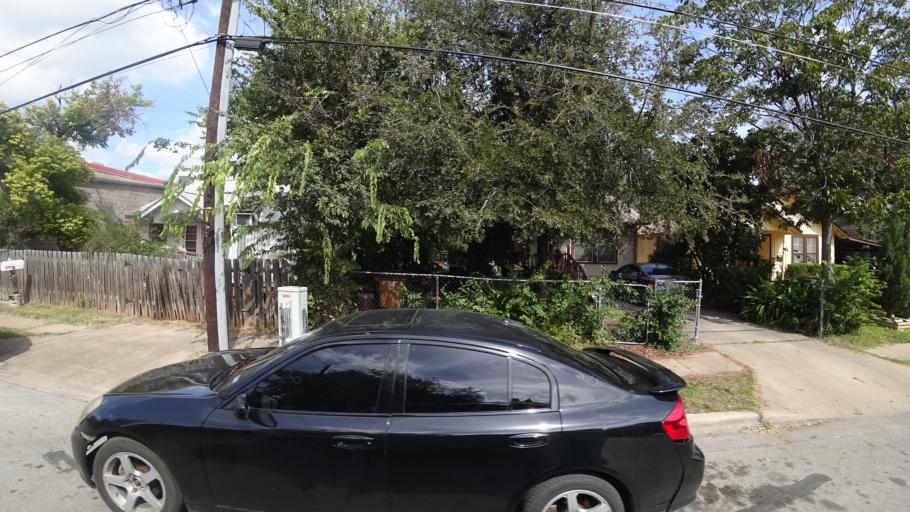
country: US
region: Texas
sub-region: Travis County
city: Austin
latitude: 30.2602
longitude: -97.7134
